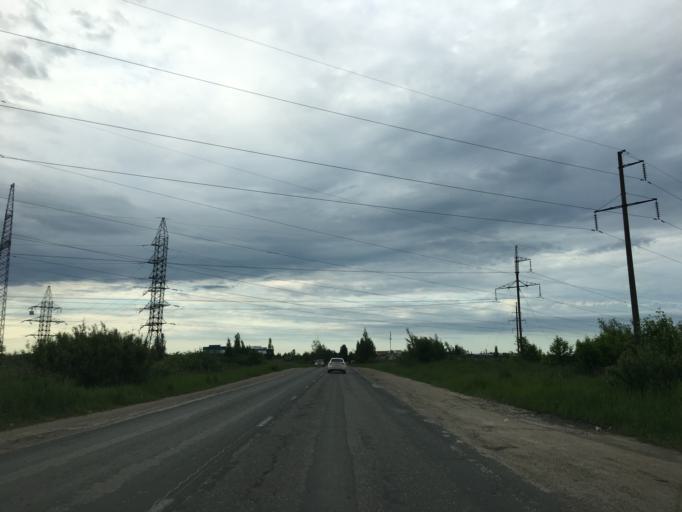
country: RU
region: Pskov
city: Pskov
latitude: 57.8455
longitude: 28.3061
